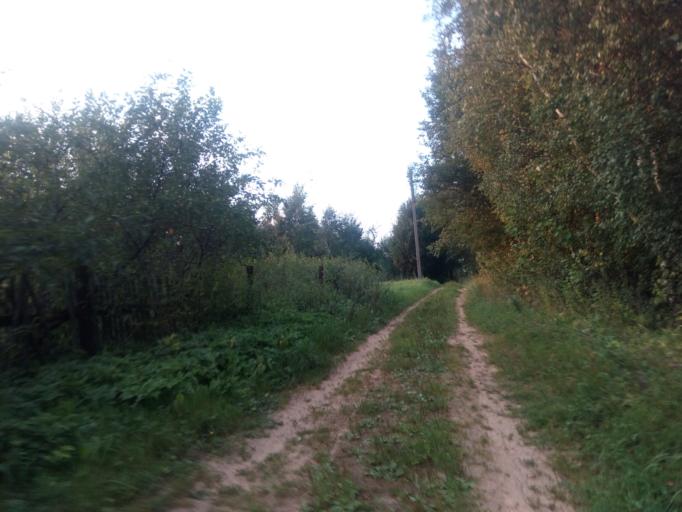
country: BY
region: Vitebsk
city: Dzisna
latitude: 55.6578
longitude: 28.3304
